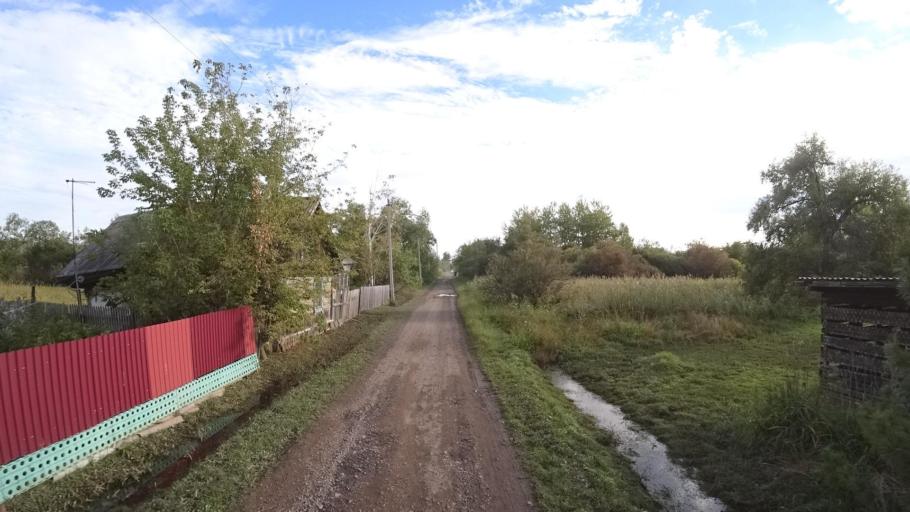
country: RU
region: Primorskiy
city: Dostoyevka
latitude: 44.2930
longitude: 133.4298
